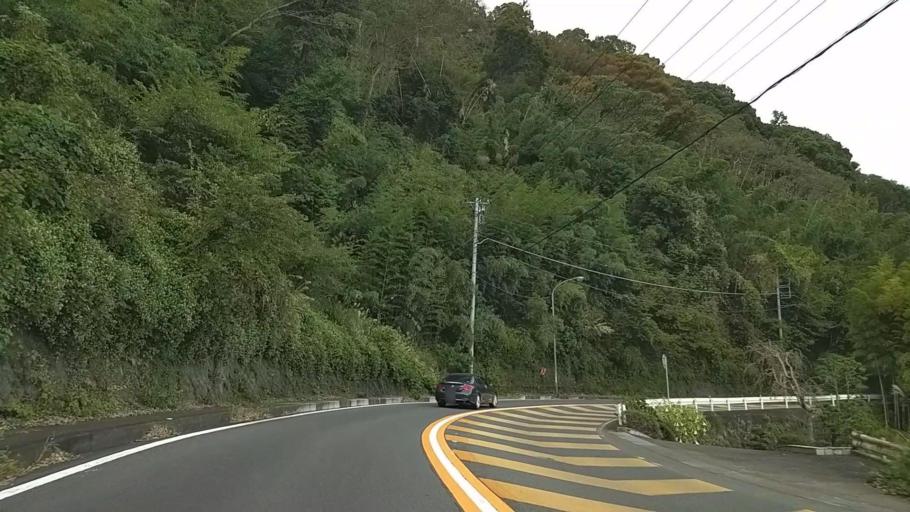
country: JP
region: Shizuoka
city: Atami
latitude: 35.1206
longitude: 139.0962
